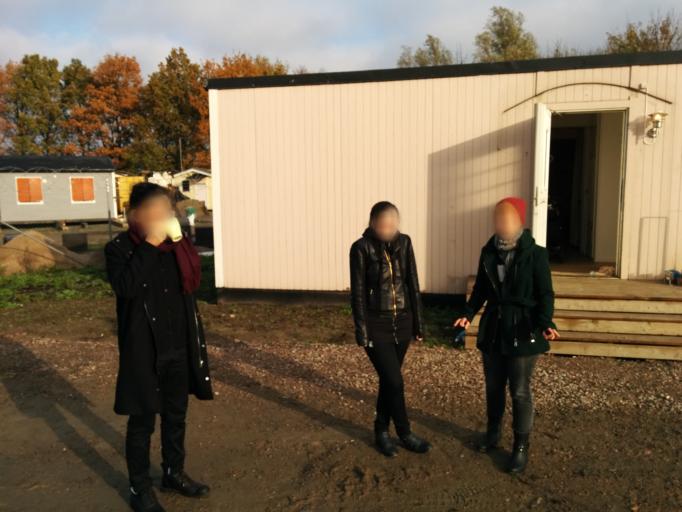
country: SE
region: Skane
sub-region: Malmo
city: Tygelsjo
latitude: 55.5525
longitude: 13.0209
